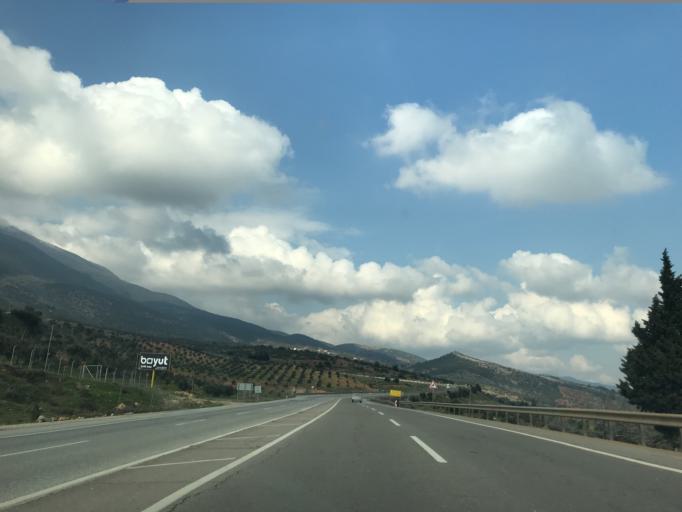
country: TR
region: Hatay
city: Kirikhan
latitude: 36.4809
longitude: 36.2775
